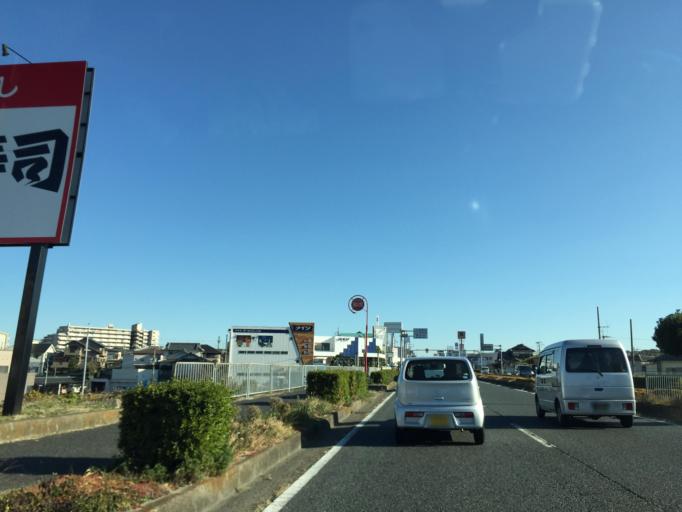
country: JP
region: Osaka
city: Kaizuka
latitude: 34.4262
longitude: 135.3437
